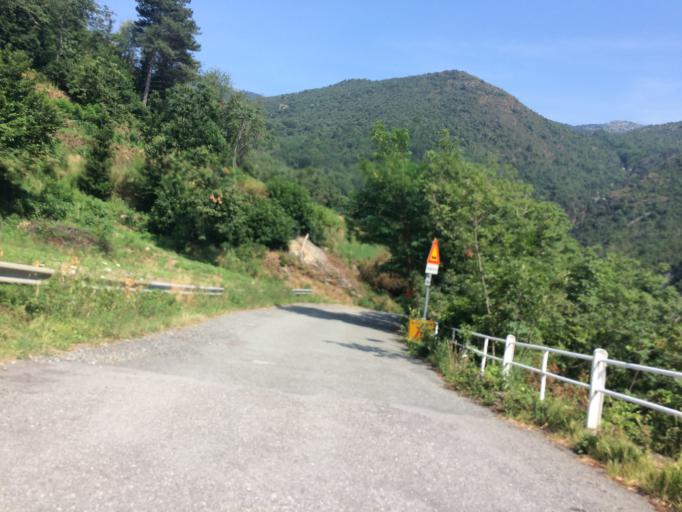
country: IT
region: Liguria
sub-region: Provincia di Genova
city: Sciarborasca
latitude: 44.4016
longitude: 8.5754
